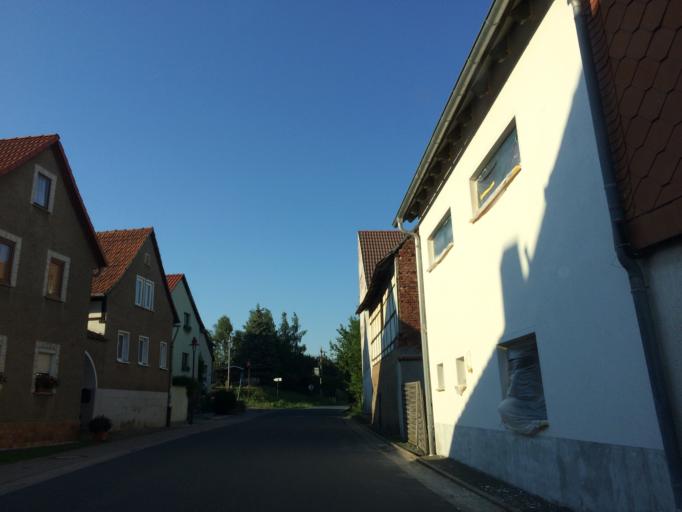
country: DE
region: Thuringia
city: Gossitz
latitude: 50.6229
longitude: 11.5864
